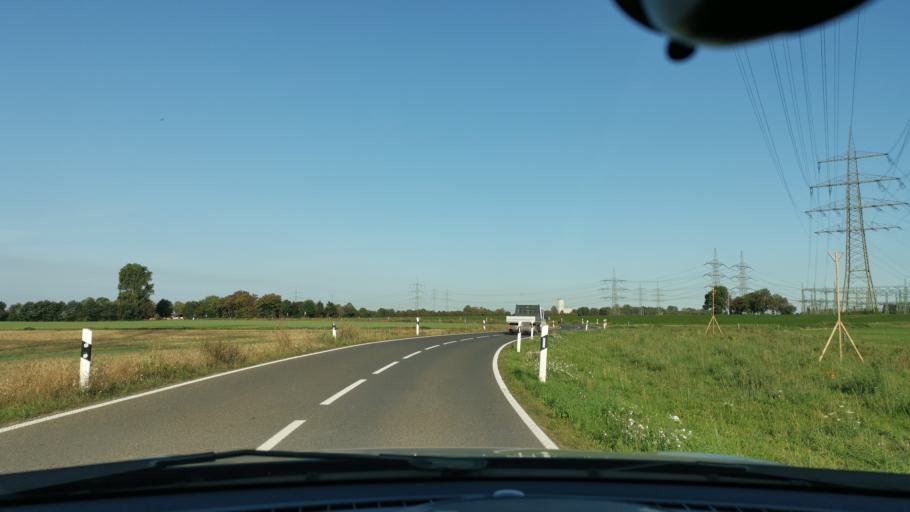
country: DE
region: North Rhine-Westphalia
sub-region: Regierungsbezirk Dusseldorf
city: Rommerskirchen
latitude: 51.0855
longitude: 6.7121
